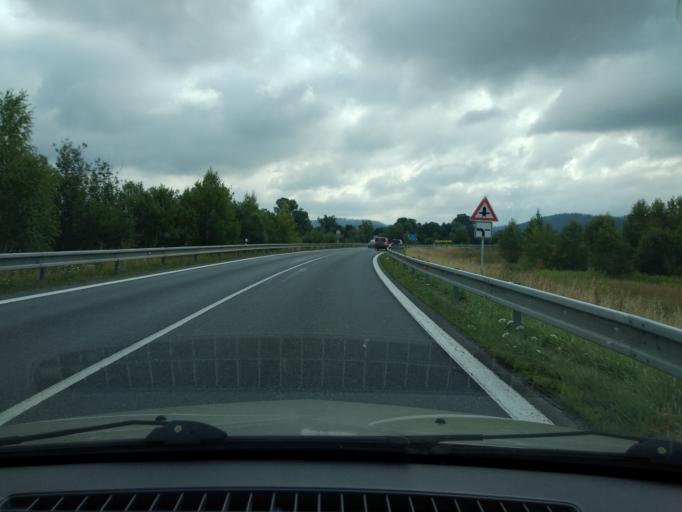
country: CZ
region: Olomoucky
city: Postrelmov
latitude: 49.9168
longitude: 16.9154
